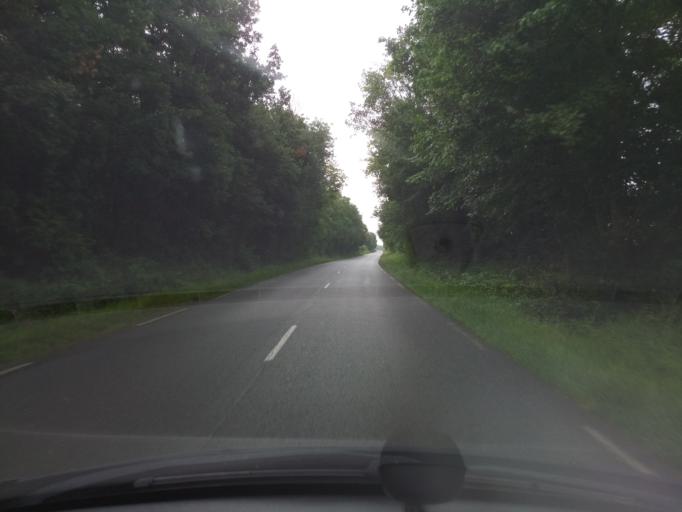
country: FR
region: Poitou-Charentes
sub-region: Departement de la Charente-Maritime
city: Courcon
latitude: 46.1807
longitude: -0.8518
